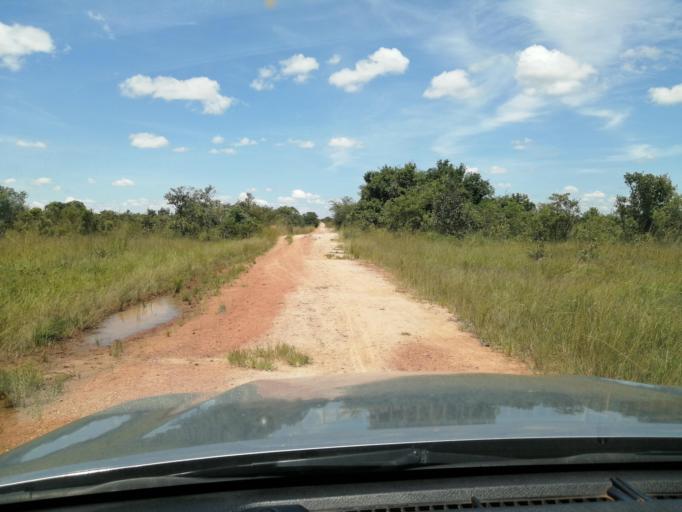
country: ZM
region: Central
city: Chibombo
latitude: -15.1156
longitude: 27.8583
